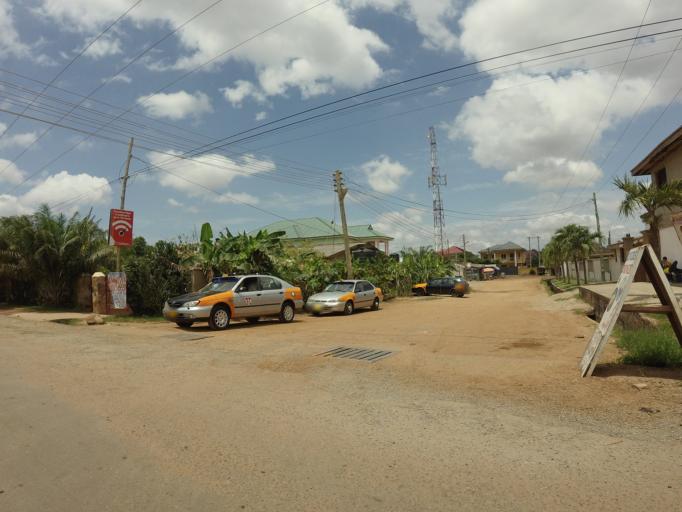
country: GH
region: Greater Accra
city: Medina Estates
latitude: 5.6816
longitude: -0.2015
